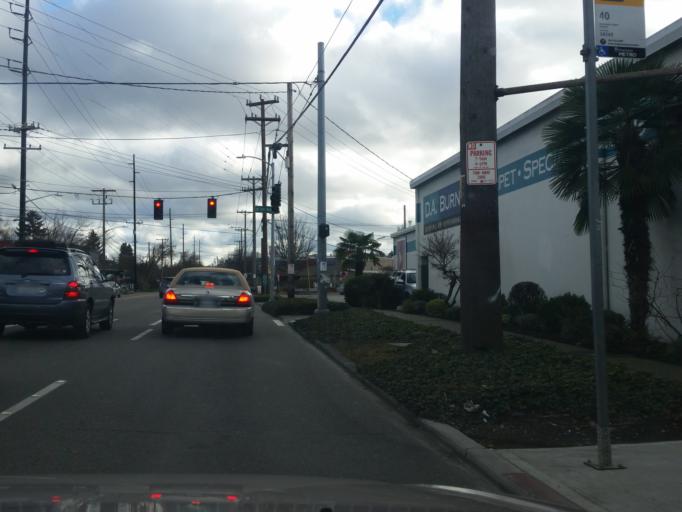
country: US
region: Washington
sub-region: King County
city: Seattle
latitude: 47.6610
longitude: -122.3668
